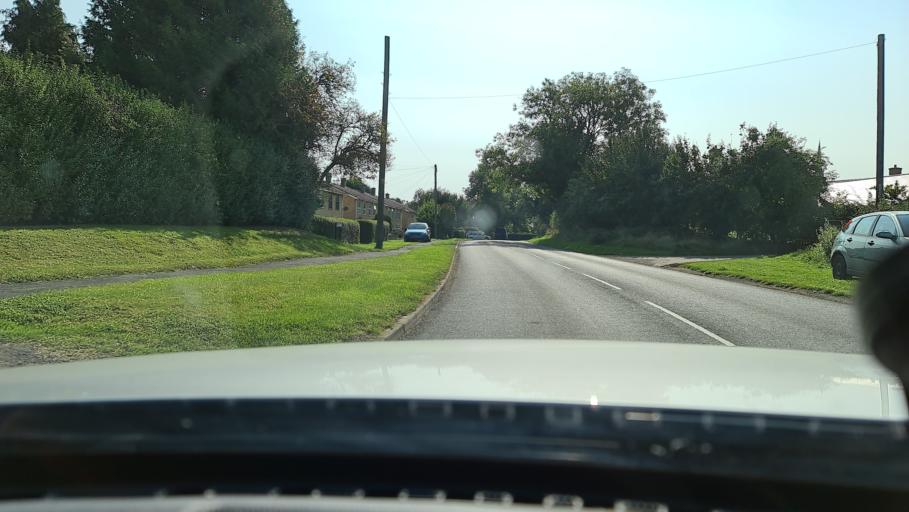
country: GB
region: England
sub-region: Oxfordshire
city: Adderbury
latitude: 52.0256
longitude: -1.2787
